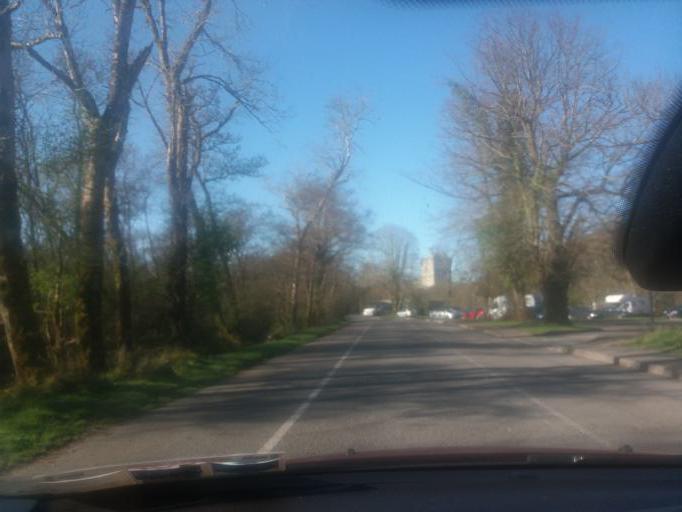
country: IE
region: Munster
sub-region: Ciarrai
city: Cill Airne
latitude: 52.0434
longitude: -9.5294
